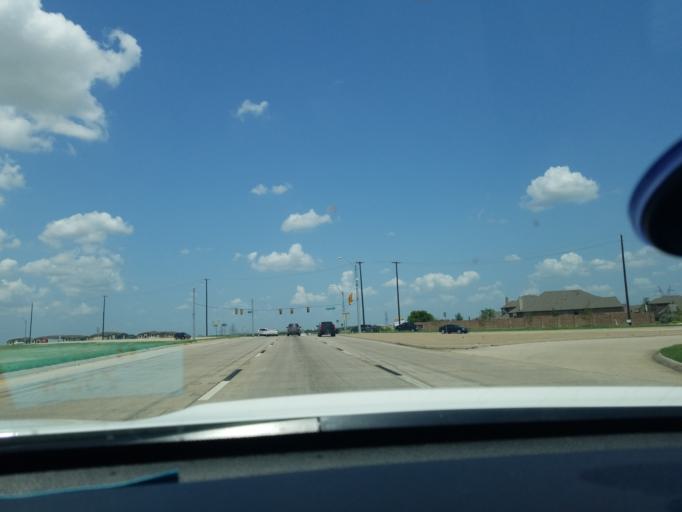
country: US
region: Texas
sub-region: Tarrant County
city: Haslet
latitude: 32.9625
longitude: -97.2992
